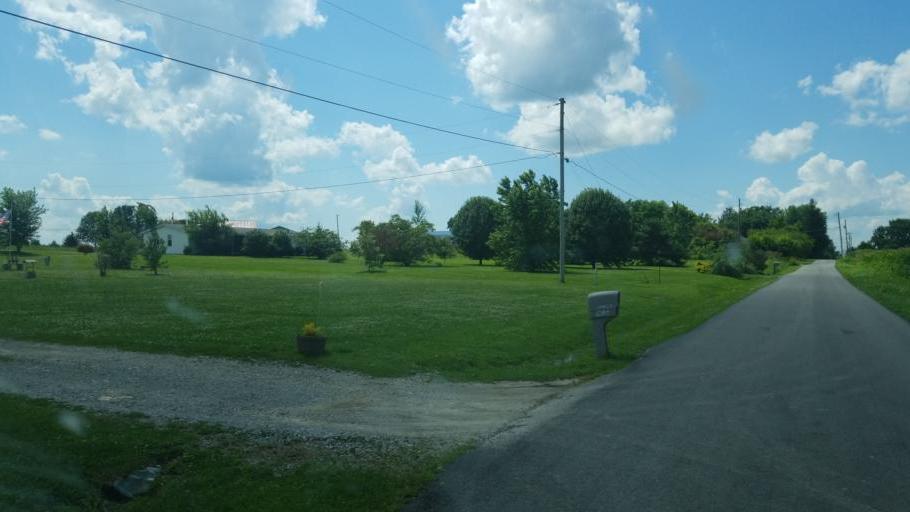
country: US
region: Ohio
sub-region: Highland County
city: Greenfield
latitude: 39.2603
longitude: -83.4399
